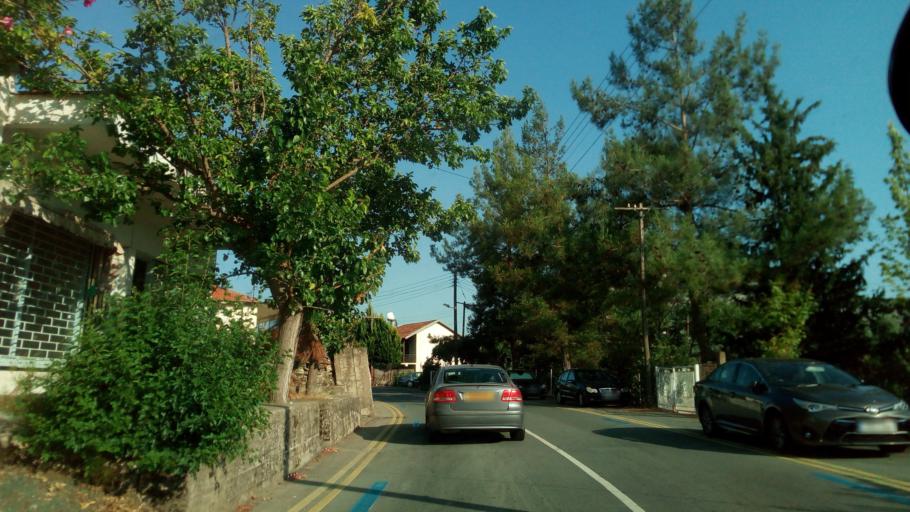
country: CY
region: Limassol
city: Pelendri
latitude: 34.8604
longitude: 32.8735
